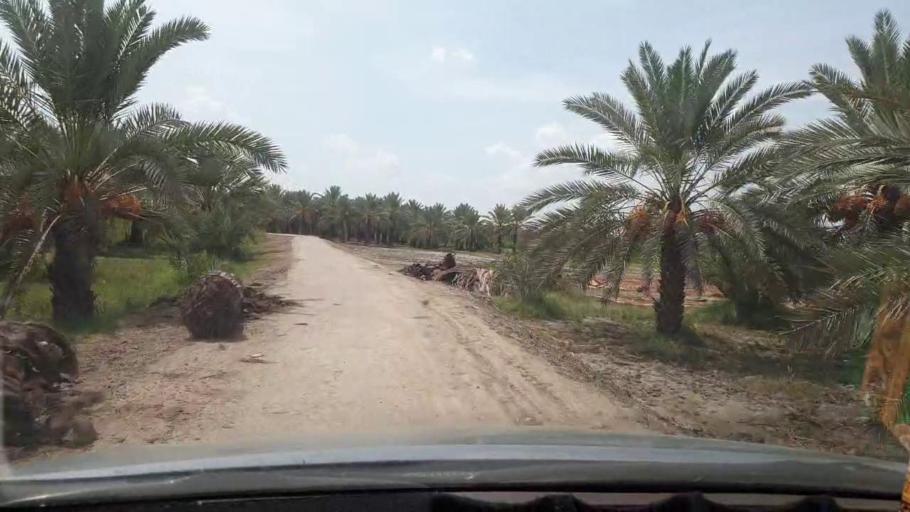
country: PK
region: Sindh
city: Khairpur
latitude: 27.4610
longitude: 68.8200
